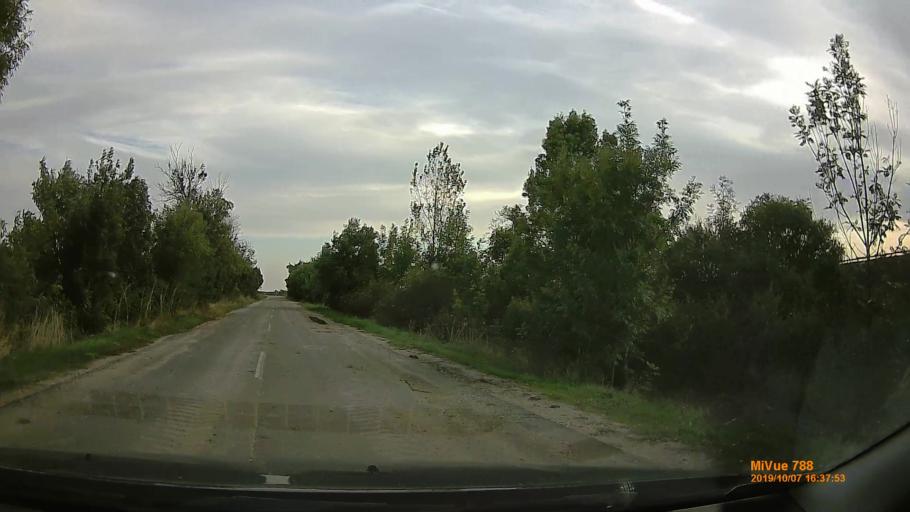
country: HU
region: Bekes
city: Szarvas
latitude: 46.8172
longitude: 20.6061
